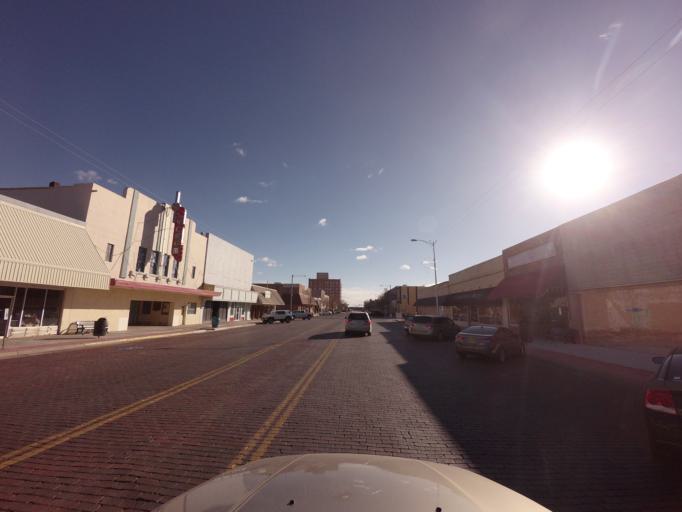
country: US
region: New Mexico
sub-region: Curry County
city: Clovis
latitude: 34.4025
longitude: -103.2054
